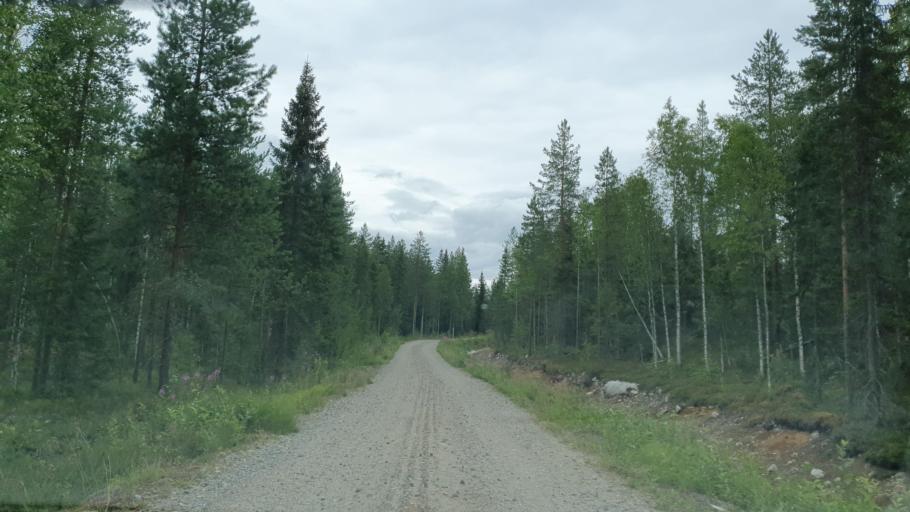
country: FI
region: Kainuu
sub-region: Kehys-Kainuu
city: Kuhmo
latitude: 64.2035
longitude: 29.3946
